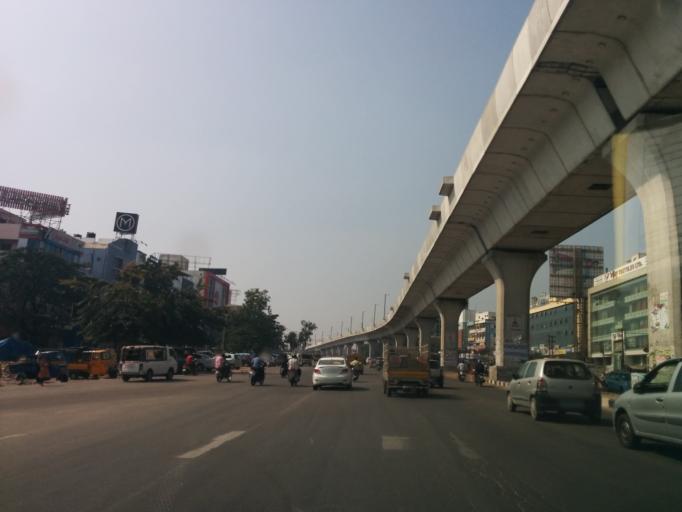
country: IN
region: Telangana
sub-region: Rangareddi
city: Kukatpalli
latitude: 17.4950
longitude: 78.3990
